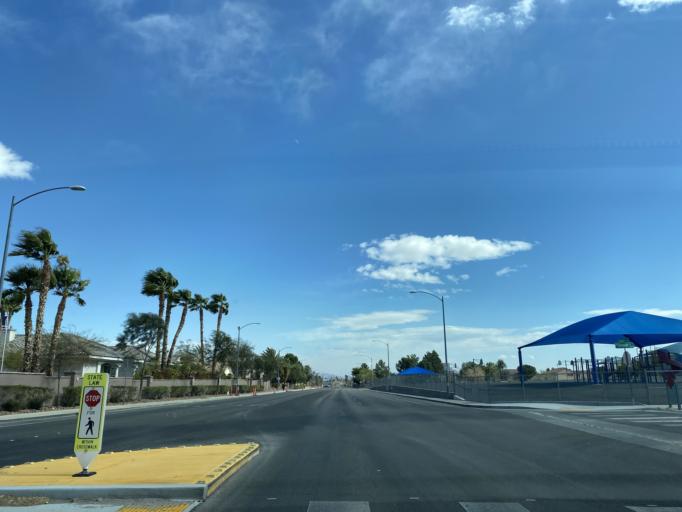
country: US
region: Nevada
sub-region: Clark County
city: Spring Valley
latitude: 36.2258
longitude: -115.2655
